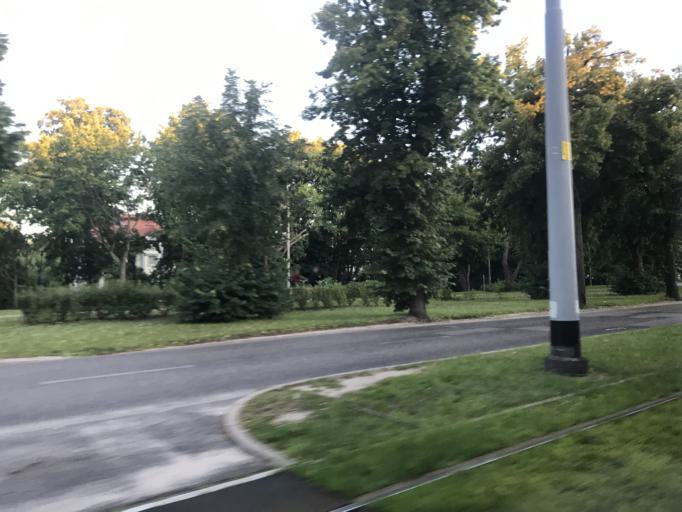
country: PL
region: Pomeranian Voivodeship
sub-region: Sopot
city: Sopot
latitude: 54.4212
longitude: 18.5872
